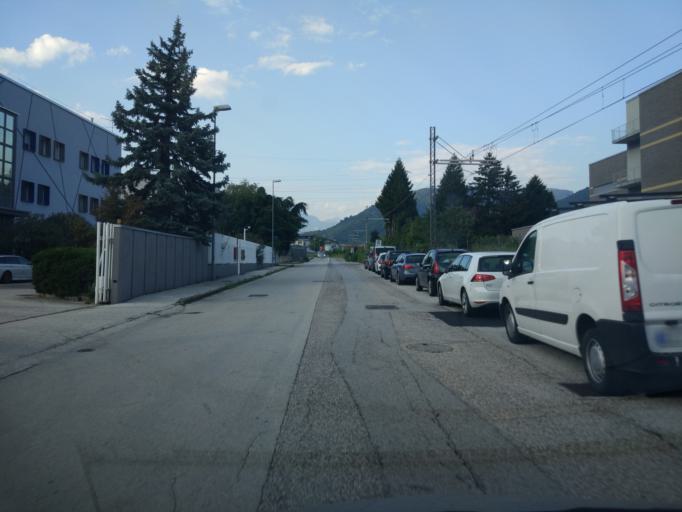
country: IT
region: Trentino-Alto Adige
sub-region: Provincia di Trento
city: Meano
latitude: 46.1278
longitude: 11.1080
